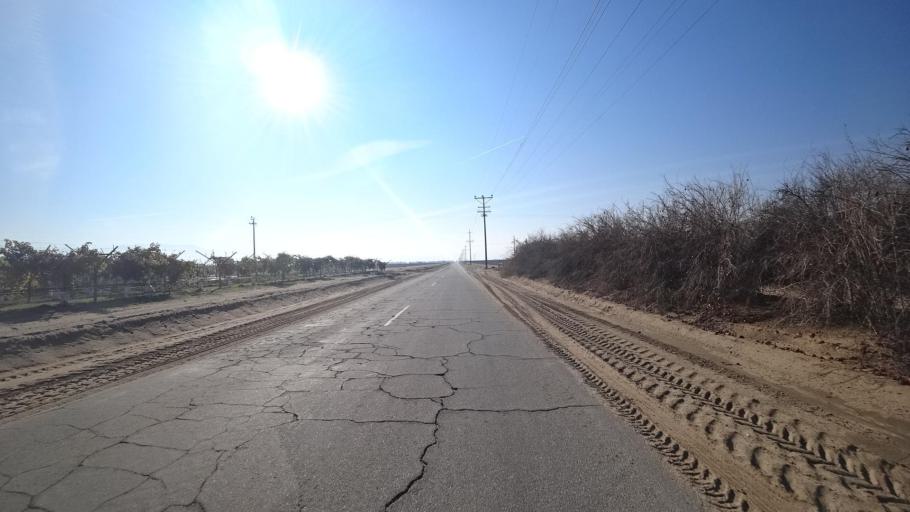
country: US
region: California
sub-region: Kern County
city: Arvin
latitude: 35.1080
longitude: -118.8778
